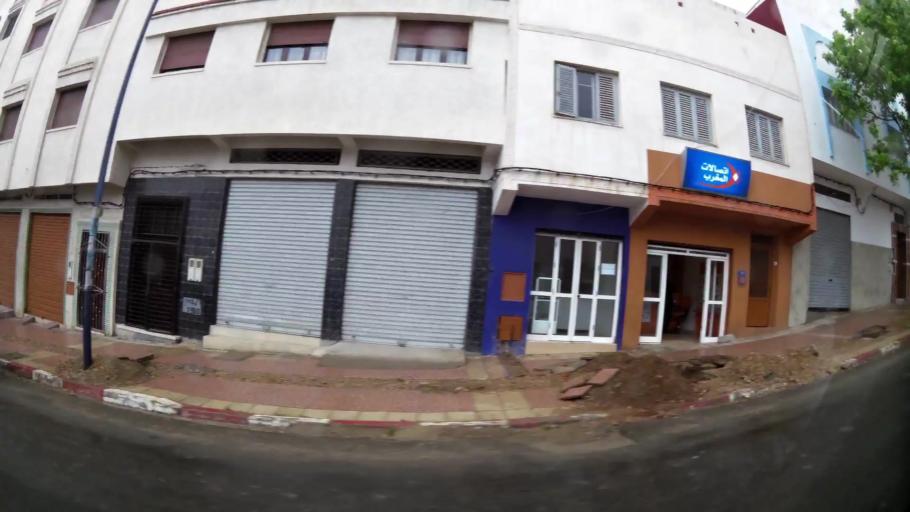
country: MA
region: Taza-Al Hoceima-Taounate
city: Al Hoceima
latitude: 35.2522
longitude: -3.9343
